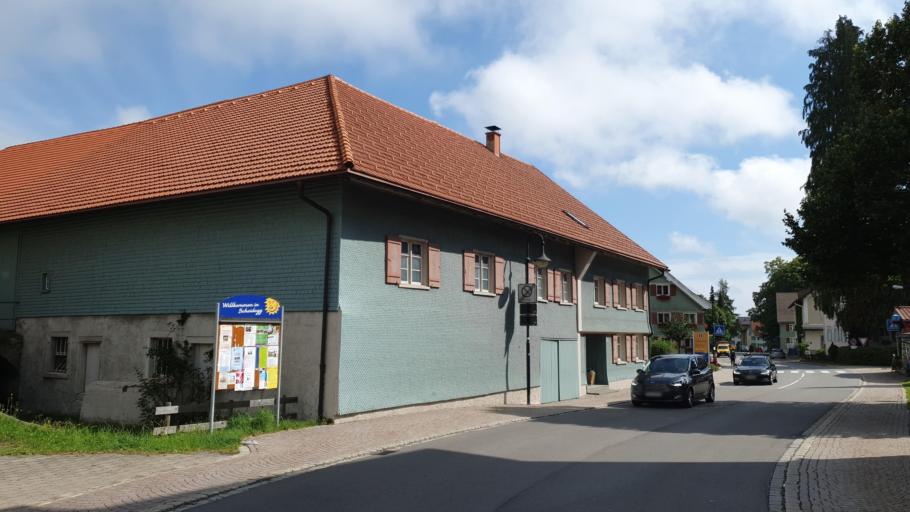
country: DE
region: Bavaria
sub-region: Swabia
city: Scheidegg
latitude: 47.5819
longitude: 9.8484
